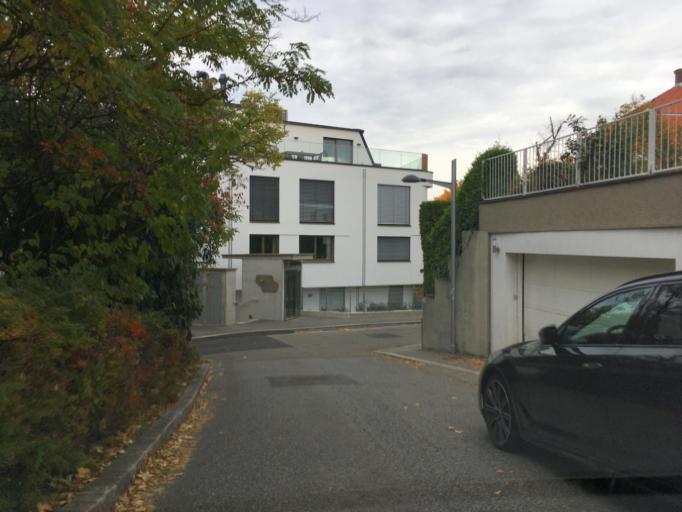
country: AT
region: Vienna
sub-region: Wien Stadt
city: Vienna
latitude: 48.2407
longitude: 16.3228
